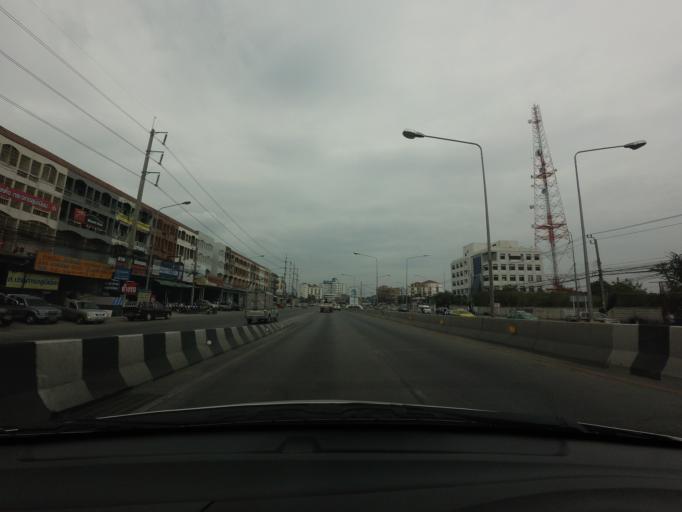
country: TH
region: Samut Prakan
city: Samut Prakan
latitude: 13.5963
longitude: 100.6096
